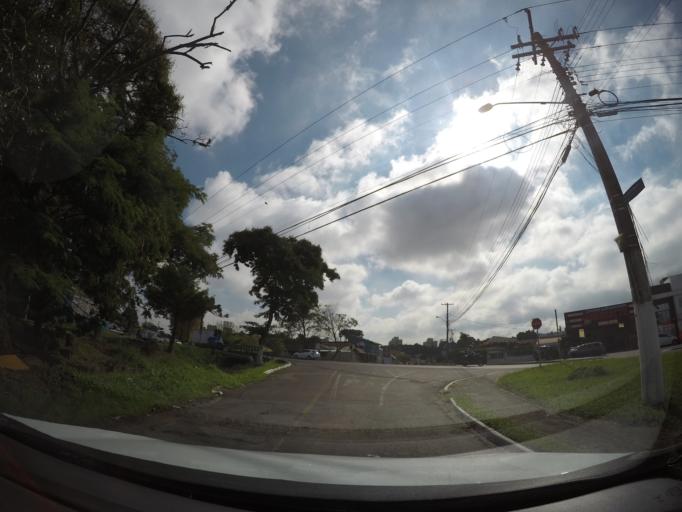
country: BR
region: Parana
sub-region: Sao Jose Dos Pinhais
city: Sao Jose dos Pinhais
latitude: -25.4920
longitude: -49.2216
